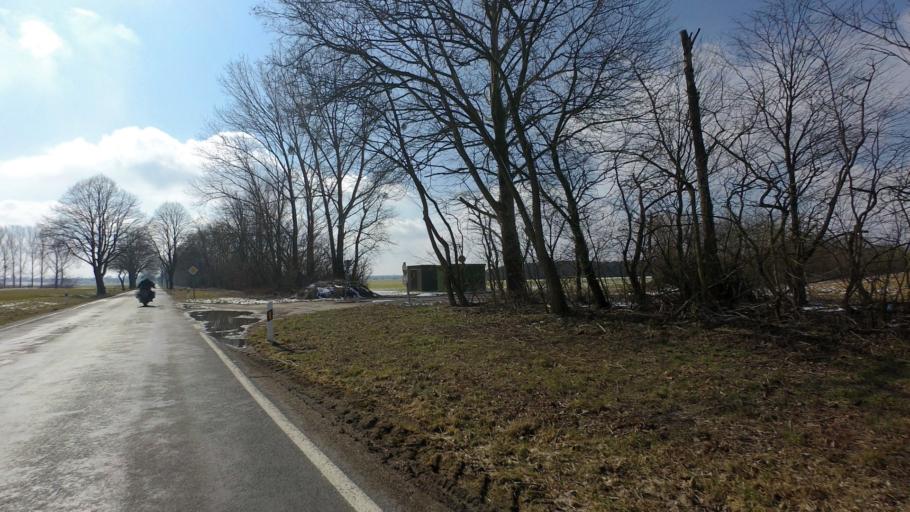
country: DE
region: Brandenburg
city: Werneuchen
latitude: 52.6968
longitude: 13.7224
